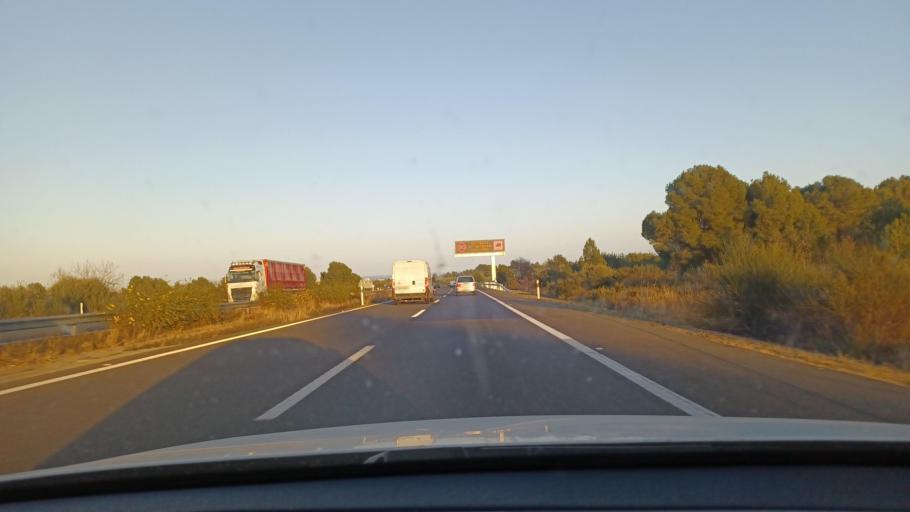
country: ES
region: Valencia
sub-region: Provincia de Castello
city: Peniscola
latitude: 40.3918
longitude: 0.3593
